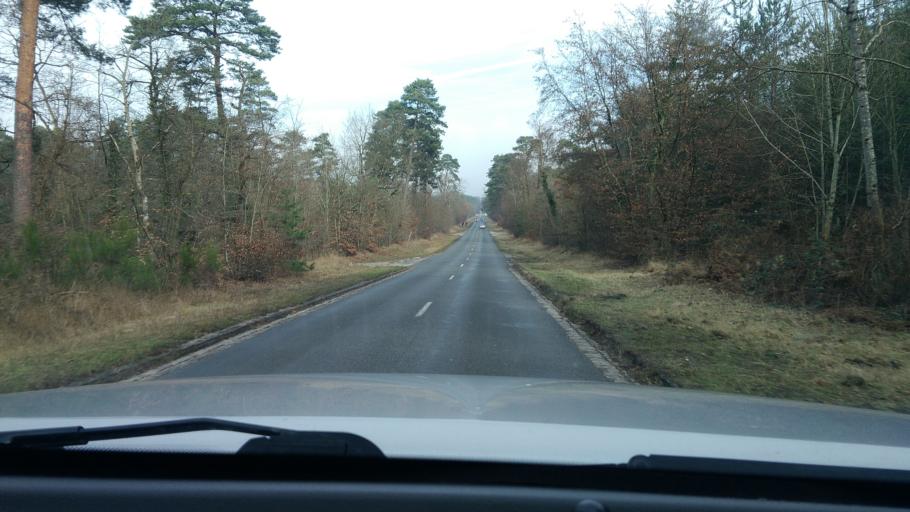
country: FR
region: Ile-de-France
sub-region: Departement de Seine-et-Marne
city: Avon
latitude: 48.4360
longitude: 2.7144
